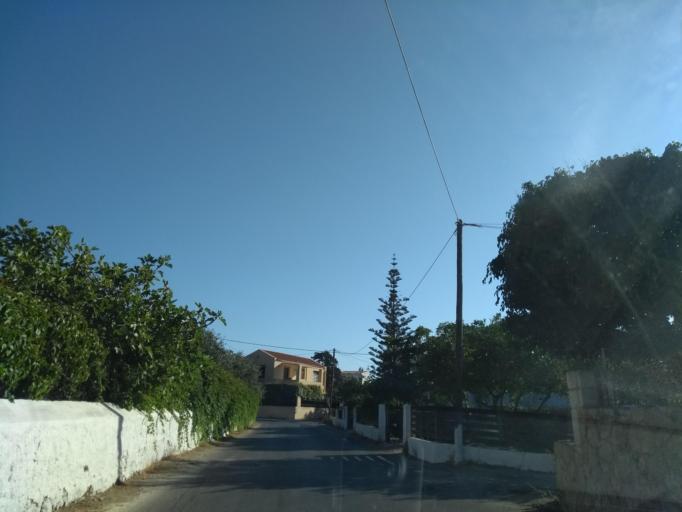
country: GR
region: Crete
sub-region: Nomos Chanias
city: Pithari
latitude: 35.5193
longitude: 24.0769
